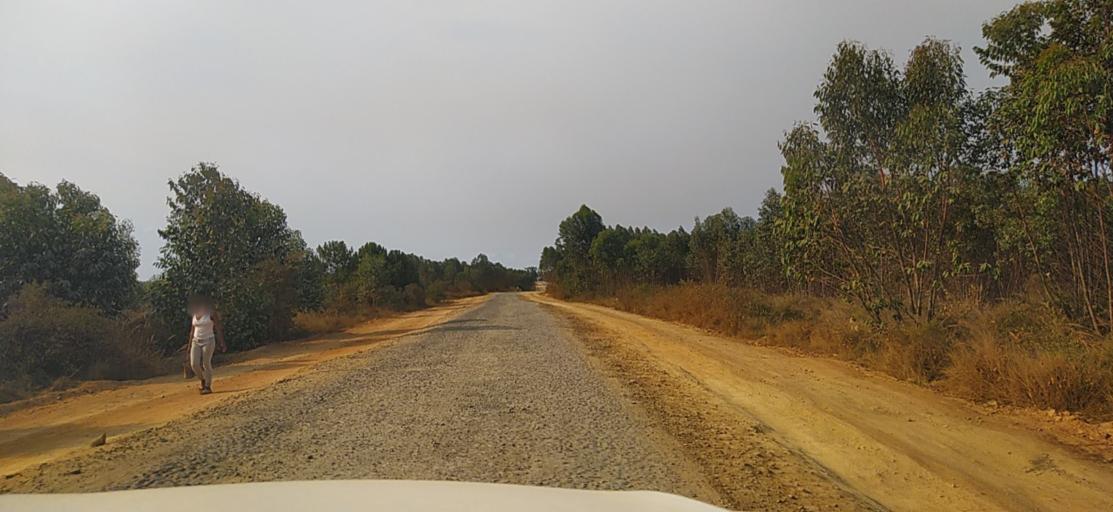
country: MG
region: Alaotra Mangoro
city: Moramanga
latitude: -18.6431
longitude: 48.2755
